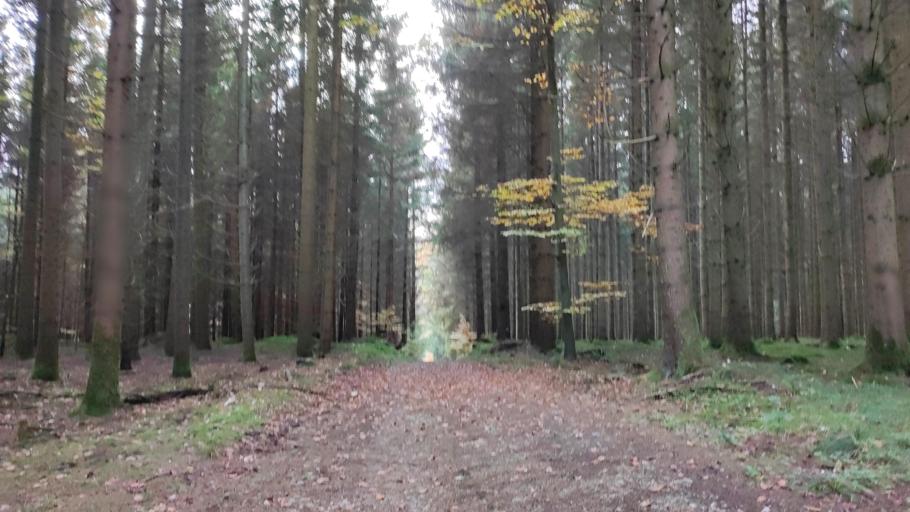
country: DE
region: Bavaria
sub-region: Swabia
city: Ziemetshausen
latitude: 48.3387
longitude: 10.5230
